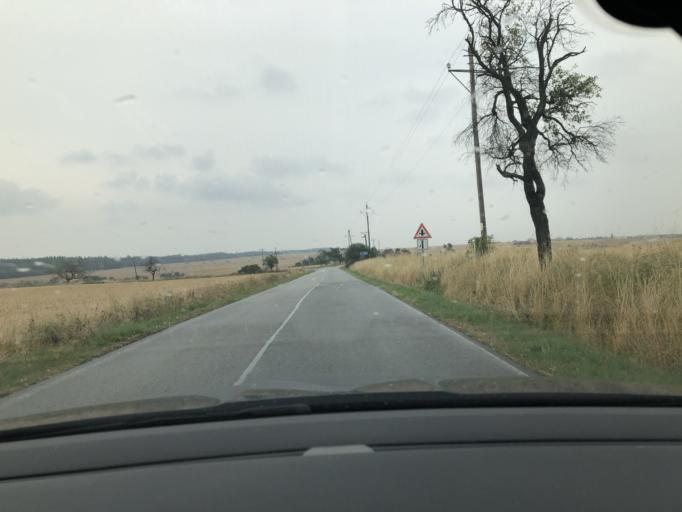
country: CZ
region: South Moravian
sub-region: Okres Znojmo
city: Jevisovice
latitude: 49.0291
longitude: 16.0263
